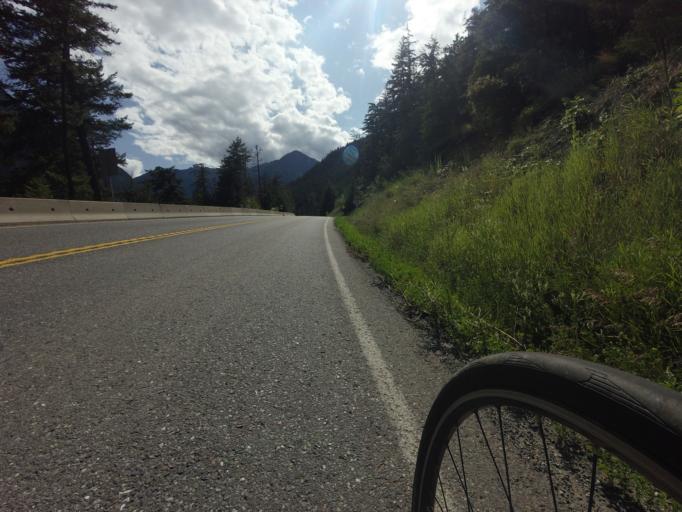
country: CA
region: British Columbia
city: Lillooet
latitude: 50.6507
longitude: -122.0174
